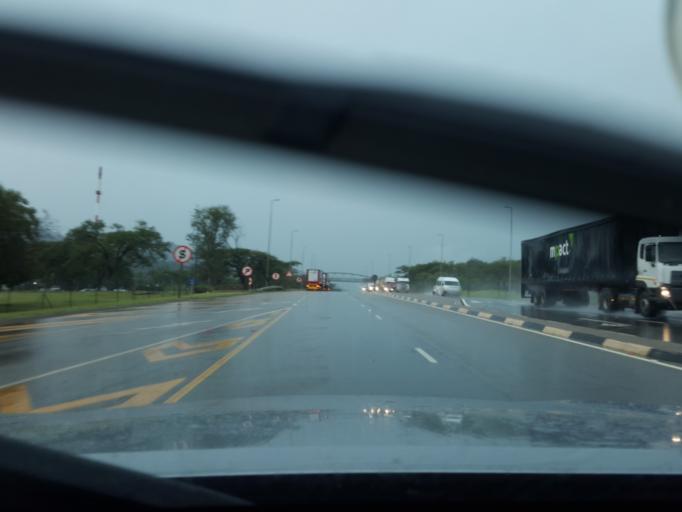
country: ZA
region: Mpumalanga
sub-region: Ehlanzeni District
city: Nelspruit
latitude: -25.5749
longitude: 30.6676
